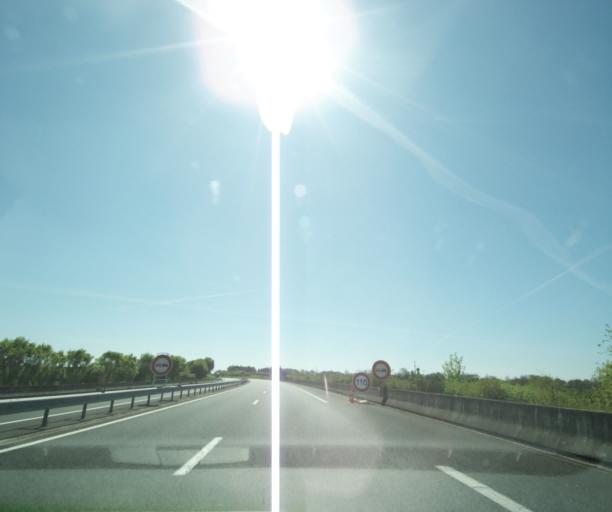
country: FR
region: Centre
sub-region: Departement de l'Indre
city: Argenton-sur-Creuse
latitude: 46.5413
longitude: 1.5071
